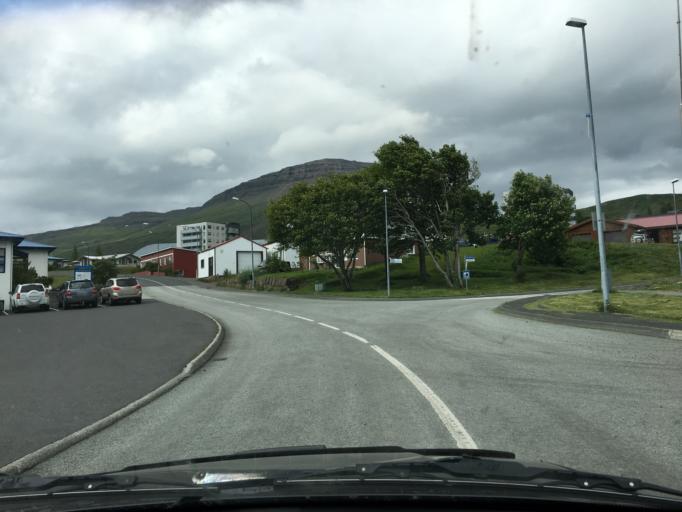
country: IS
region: East
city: Reydarfjoerdur
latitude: 65.0316
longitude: -14.2060
